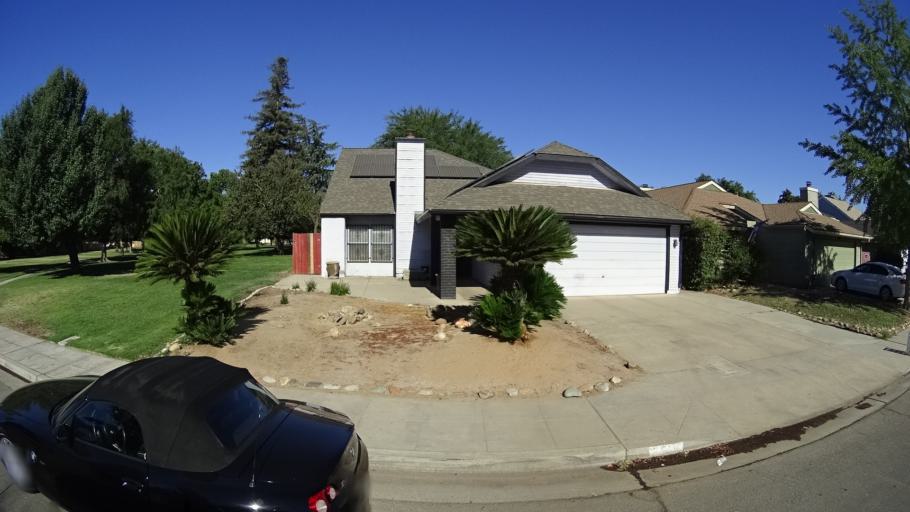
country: US
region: California
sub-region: Fresno County
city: West Park
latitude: 36.7741
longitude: -119.8572
